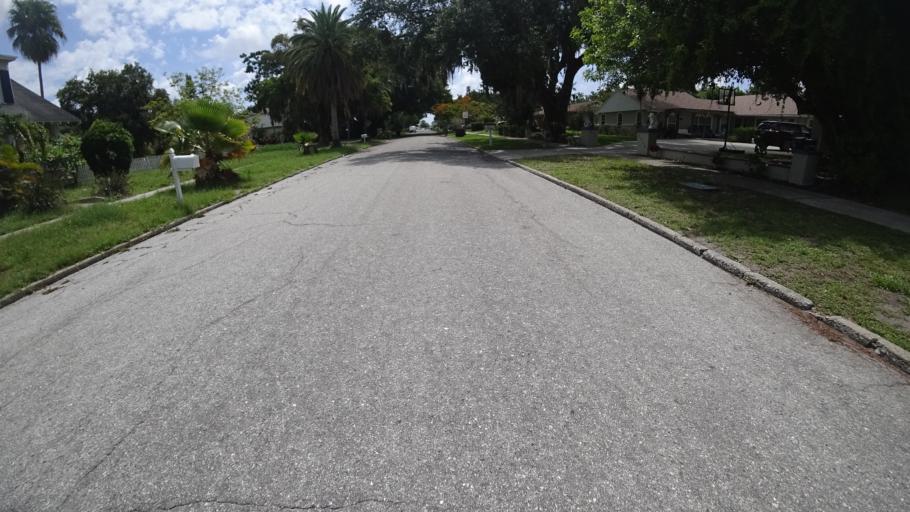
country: US
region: Florida
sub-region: Manatee County
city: Whitfield
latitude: 27.4034
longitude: -82.5704
